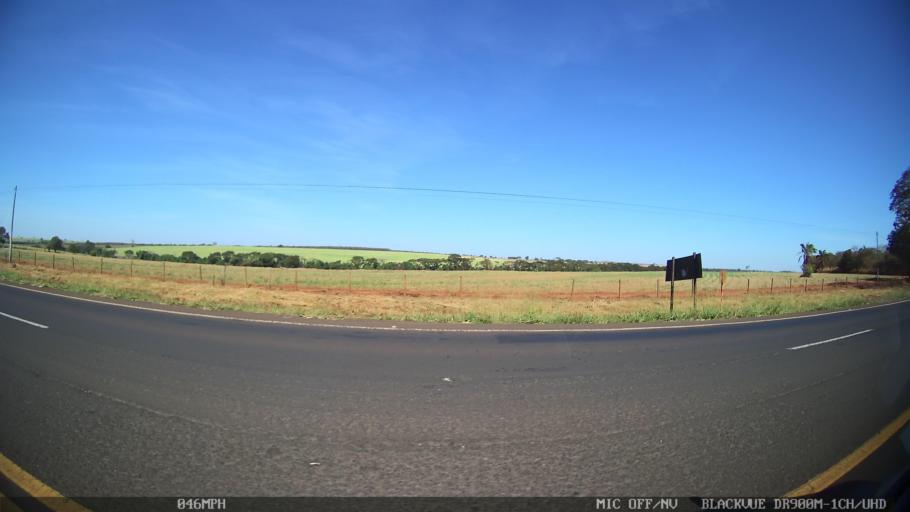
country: BR
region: Sao Paulo
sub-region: Barretos
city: Barretos
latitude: -20.5746
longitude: -48.6780
